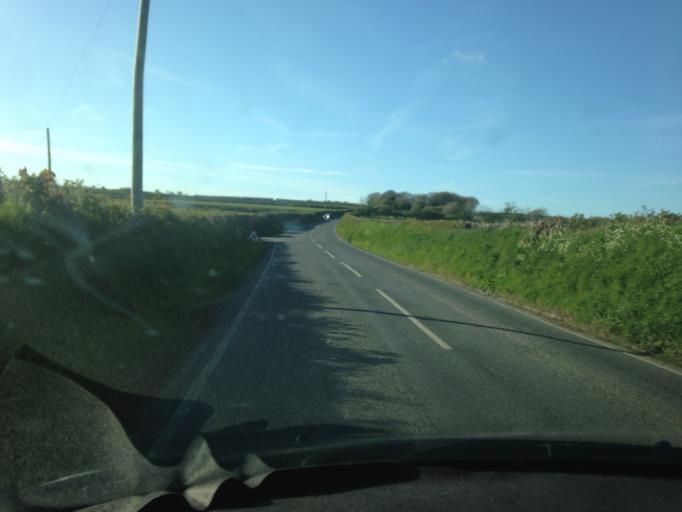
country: GB
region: Wales
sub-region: County of Ceredigion
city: Newcastle Emlyn
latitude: 52.1198
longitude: -4.4411
